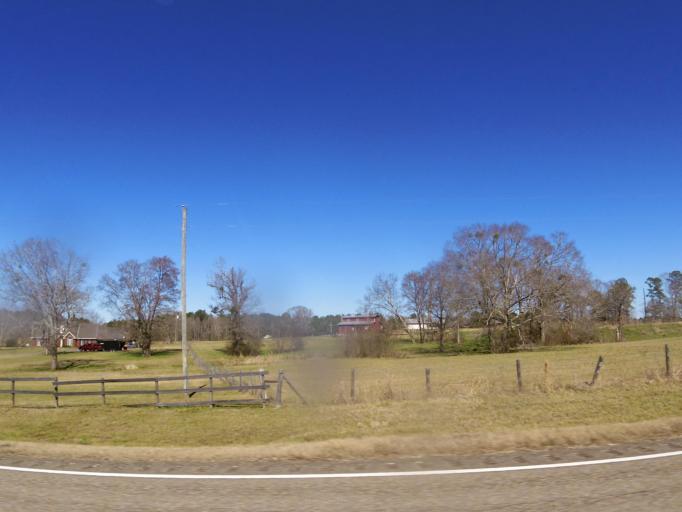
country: US
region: Alabama
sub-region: Montgomery County
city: Pike Road
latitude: 32.1825
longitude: -86.0907
